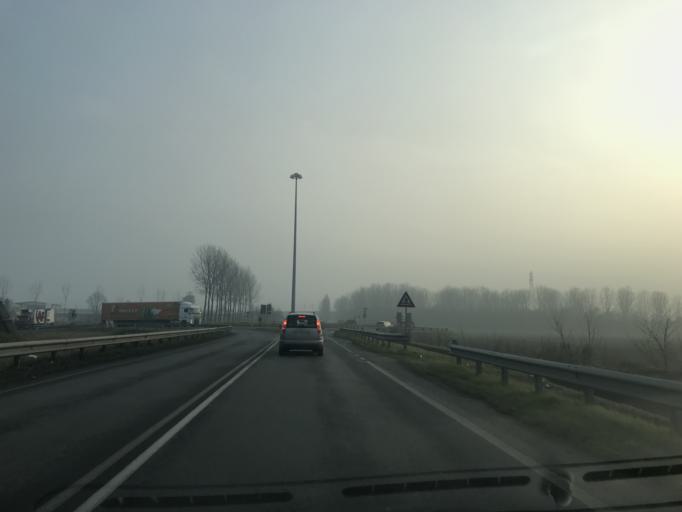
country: IT
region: Lombardy
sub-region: Provincia di Lodi
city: Villanova del Sillaro
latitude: 45.2433
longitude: 9.5009
